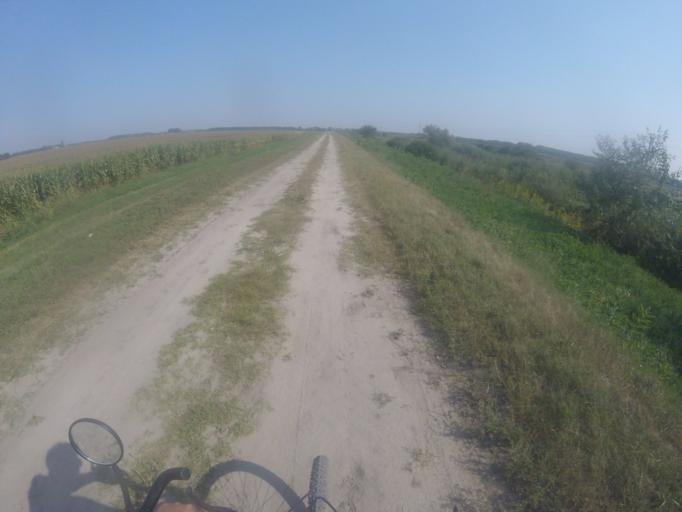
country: HU
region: Bacs-Kiskun
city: Ersekcsanad
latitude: 46.2235
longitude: 18.9580
